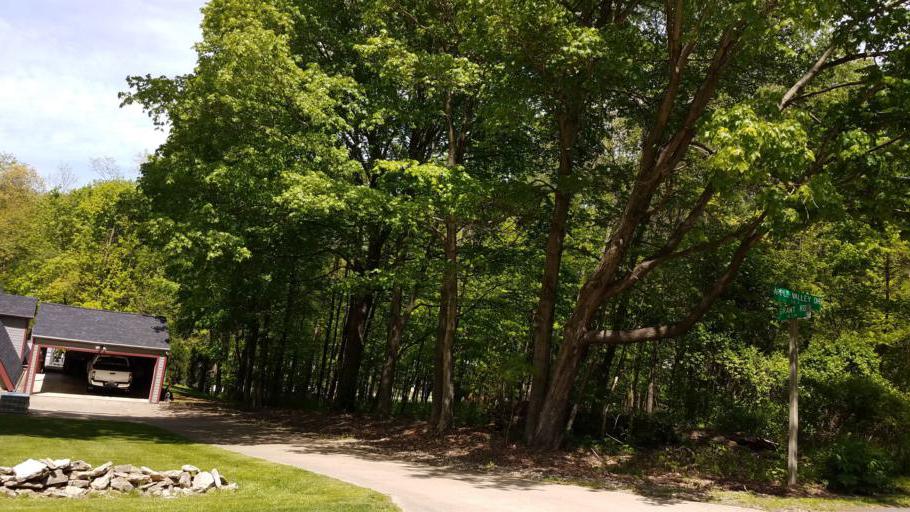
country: US
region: Ohio
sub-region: Knox County
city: Gambier
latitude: 40.4164
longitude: -82.3583
